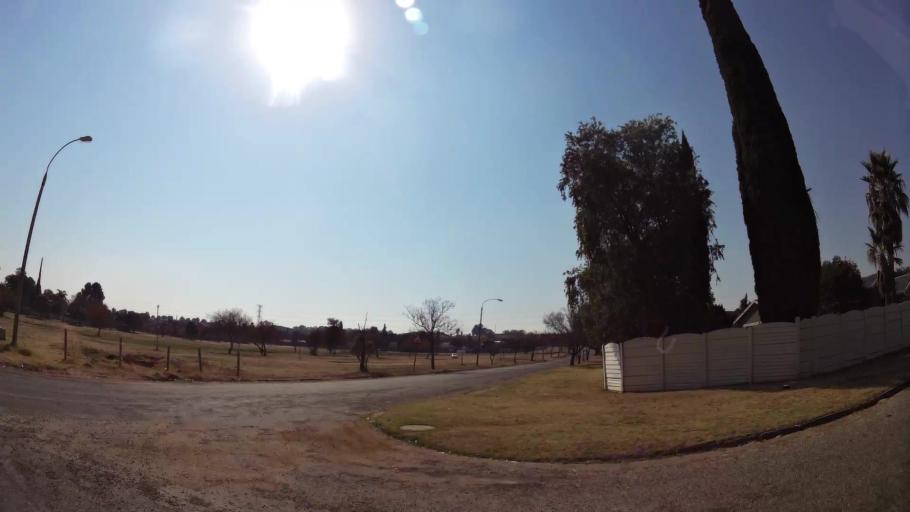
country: ZA
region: Gauteng
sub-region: Ekurhuleni Metropolitan Municipality
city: Boksburg
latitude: -26.2331
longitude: 28.2766
